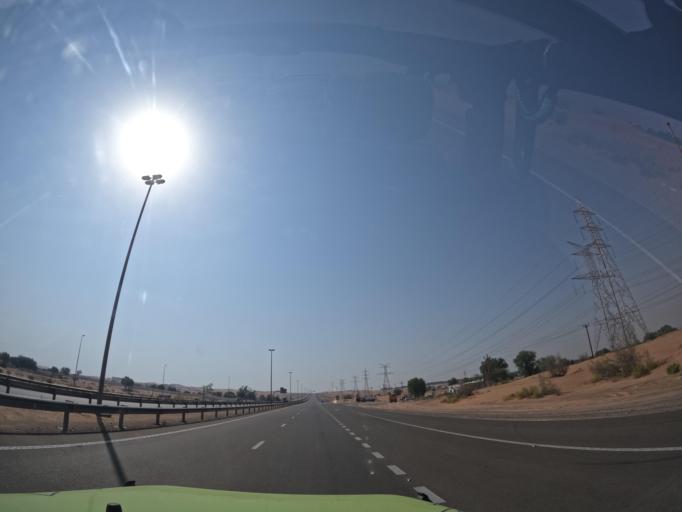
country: OM
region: Al Buraimi
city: Al Buraymi
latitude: 24.3607
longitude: 55.7316
